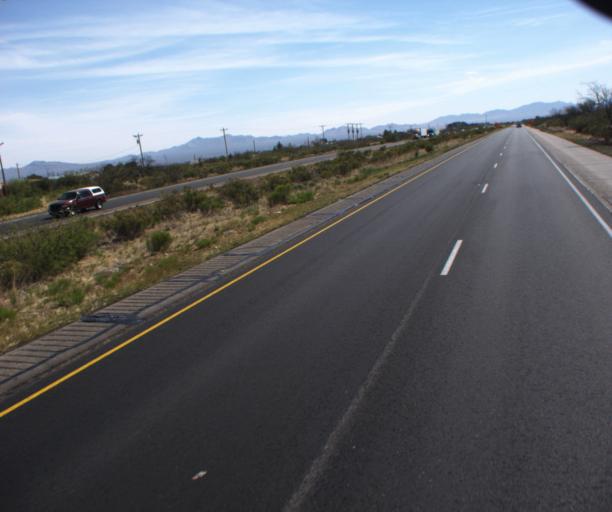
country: US
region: Arizona
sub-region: Cochise County
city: Mescal
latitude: 31.9629
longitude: -110.4098
